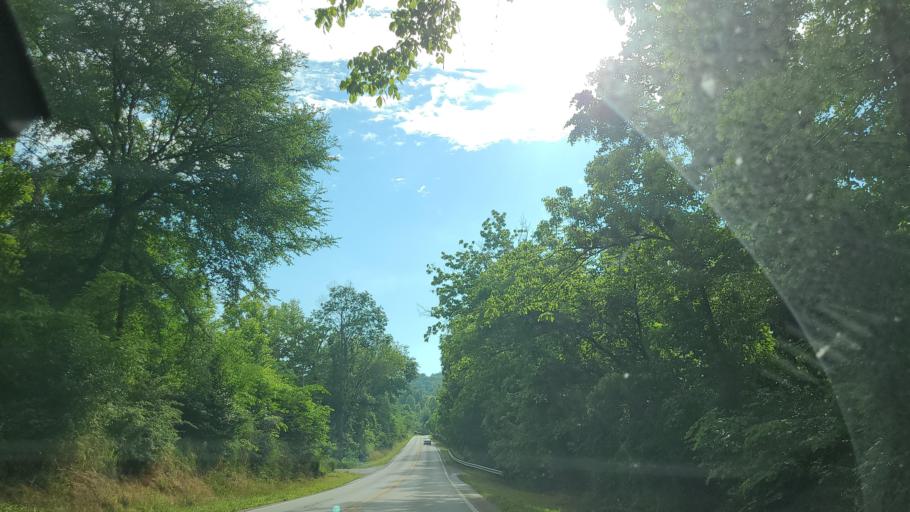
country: US
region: Kentucky
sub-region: Whitley County
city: Williamsburg
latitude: 36.7308
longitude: -84.1221
